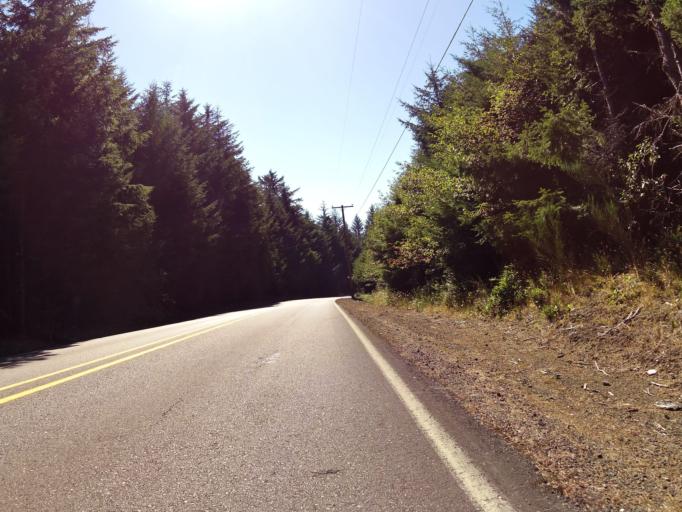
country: US
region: Oregon
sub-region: Coos County
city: Barview
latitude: 43.3201
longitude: -124.3424
